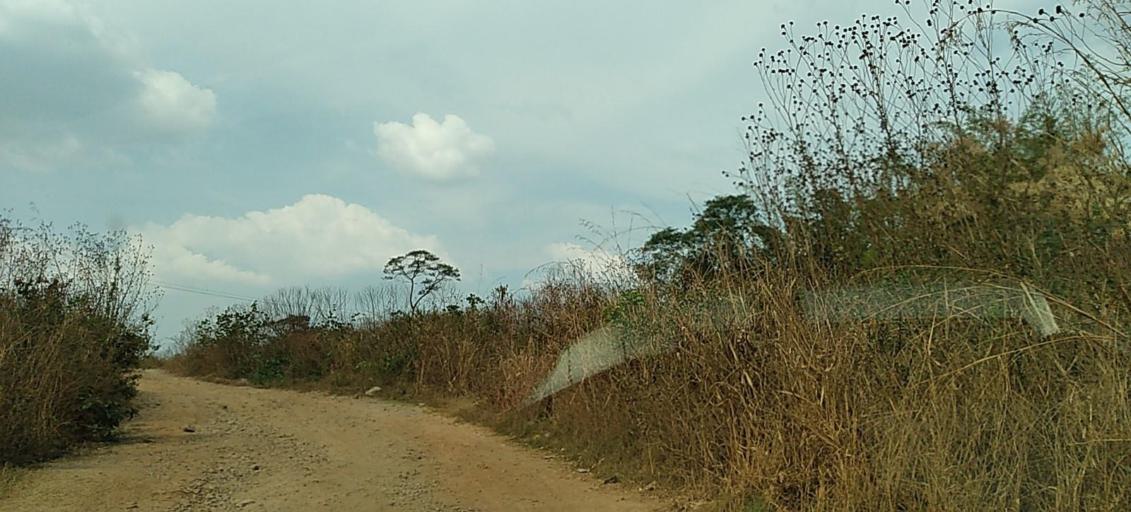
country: ZM
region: Copperbelt
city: Chililabombwe
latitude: -12.3975
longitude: 27.8039
